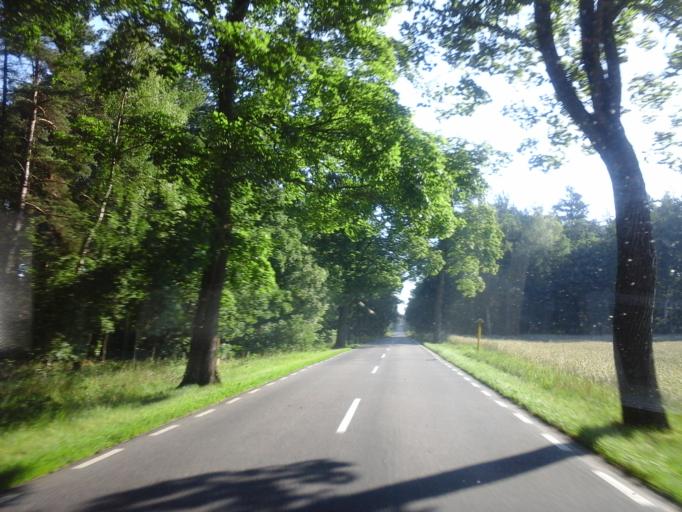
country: PL
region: West Pomeranian Voivodeship
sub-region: Powiat choszczenski
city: Recz
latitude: 53.2284
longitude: 15.4866
